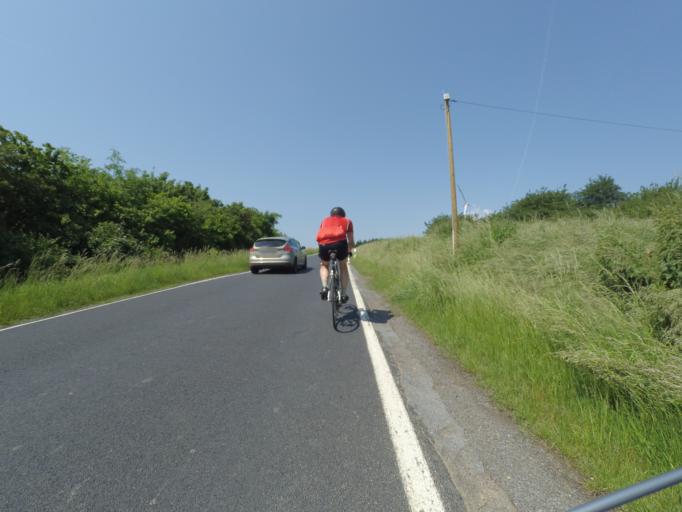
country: DE
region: Rheinland-Pfalz
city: Reudelsterz
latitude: 50.3227
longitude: 7.1519
